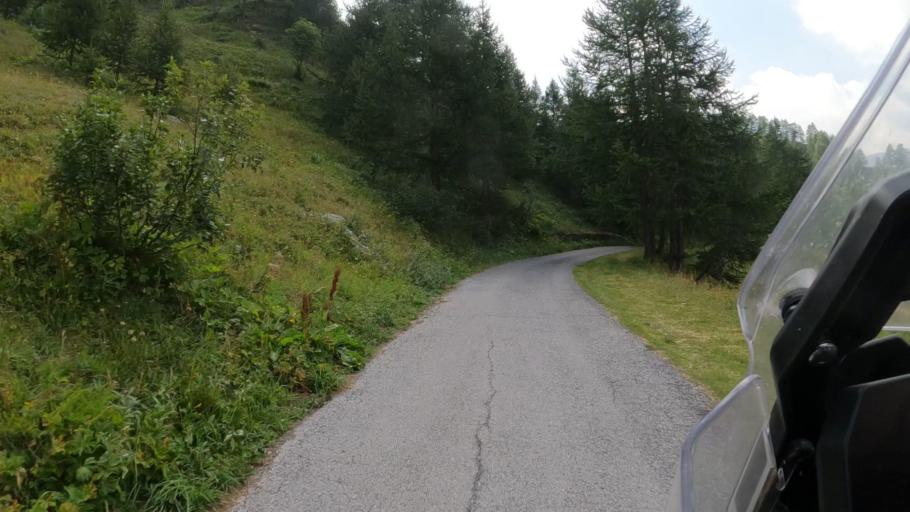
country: IT
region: Piedmont
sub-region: Provincia di Cuneo
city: Marmora
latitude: 44.4187
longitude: 7.1059
